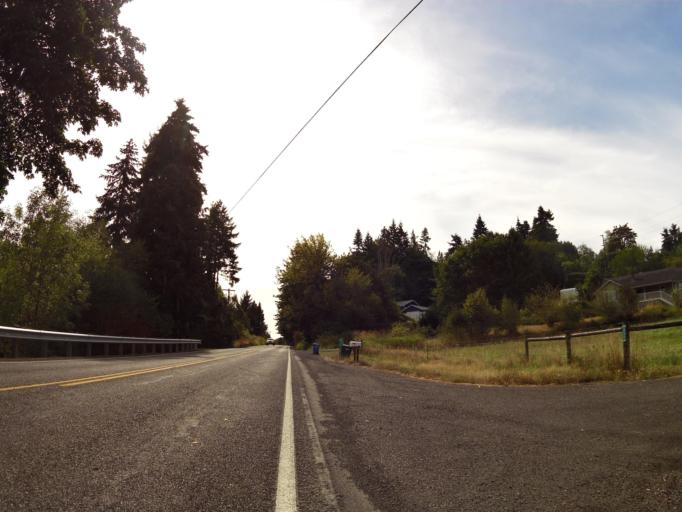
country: US
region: Washington
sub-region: Lewis County
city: Chehalis
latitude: 46.6345
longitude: -122.9708
